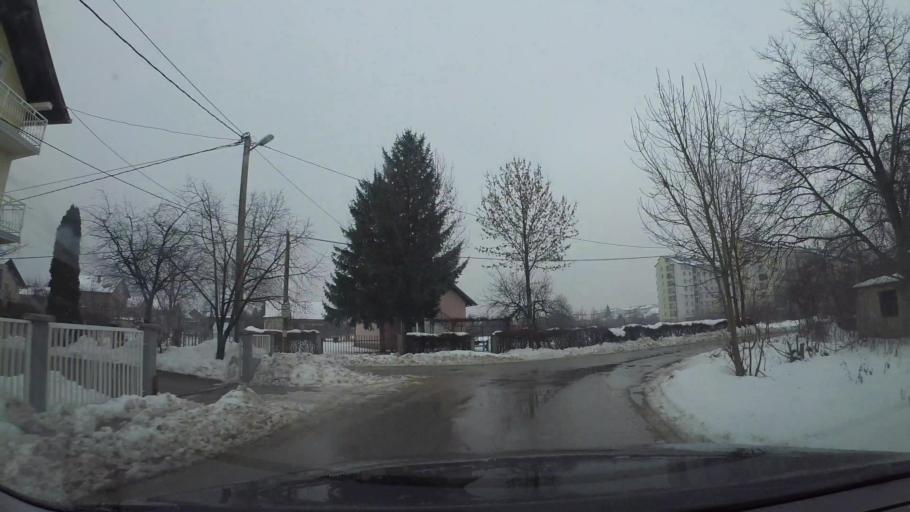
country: BA
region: Federation of Bosnia and Herzegovina
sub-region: Kanton Sarajevo
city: Sarajevo
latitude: 43.8433
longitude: 18.2990
